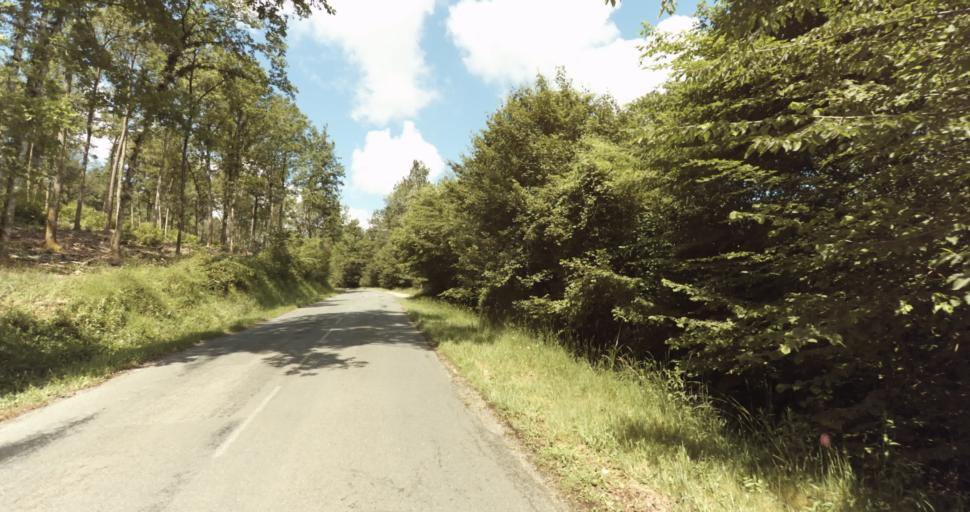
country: FR
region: Aquitaine
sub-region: Departement de la Dordogne
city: Beaumont-du-Perigord
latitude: 44.8124
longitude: 0.8611
